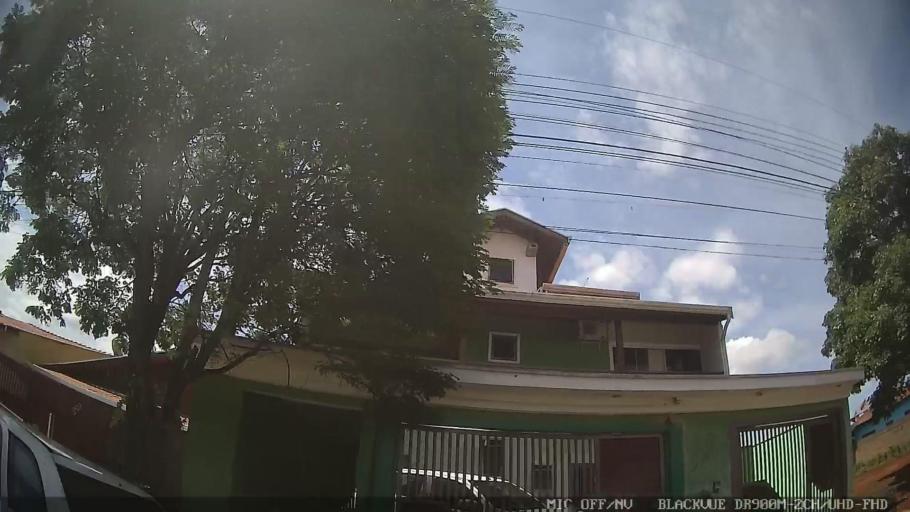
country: BR
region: Sao Paulo
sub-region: Artur Nogueira
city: Artur Nogueira
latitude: -22.6111
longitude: -47.0676
